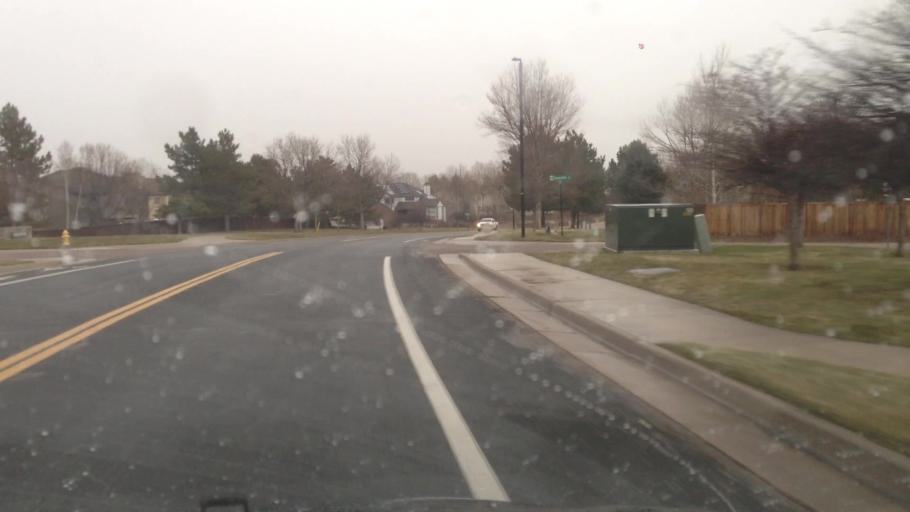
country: US
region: Colorado
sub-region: Douglas County
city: Stonegate
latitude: 39.5241
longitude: -104.7979
